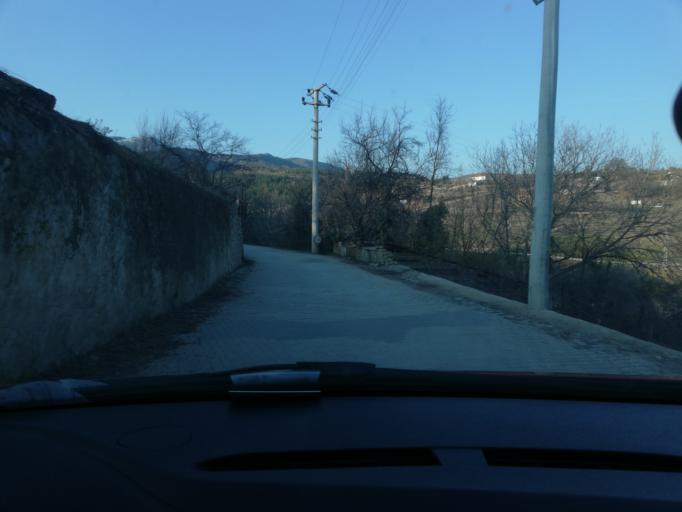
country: TR
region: Karabuk
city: Safranbolu
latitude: 41.2833
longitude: 32.6784
